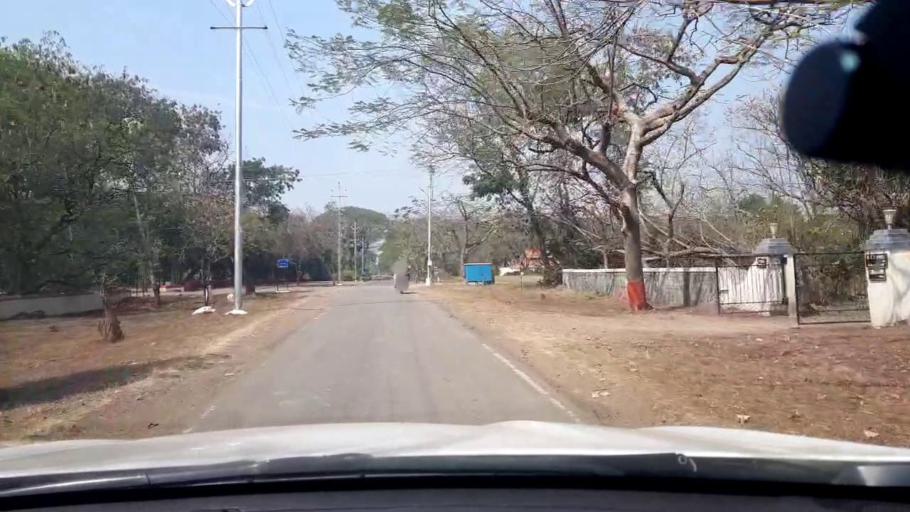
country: IN
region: Maharashtra
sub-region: Pune Division
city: Shivaji Nagar
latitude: 18.5439
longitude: 73.8655
